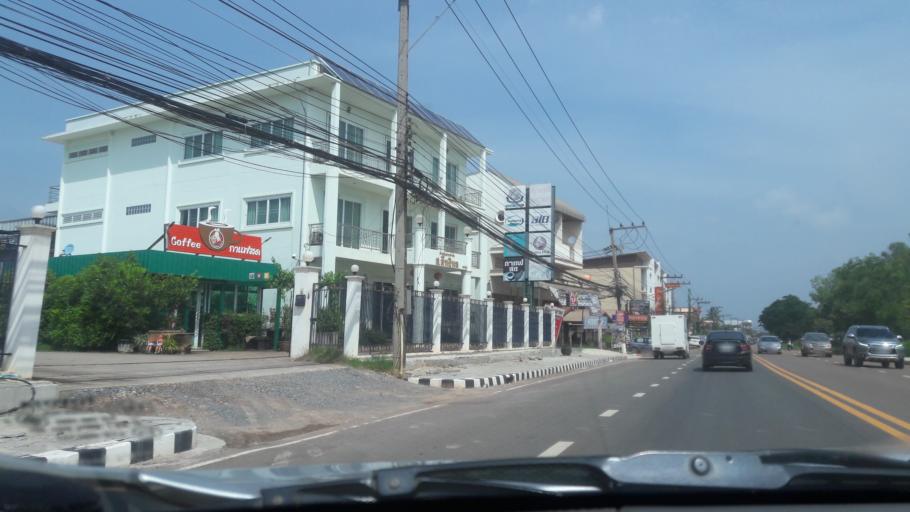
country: TH
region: Changwat Udon Thani
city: Udon Thani
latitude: 17.4304
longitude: 102.8191
